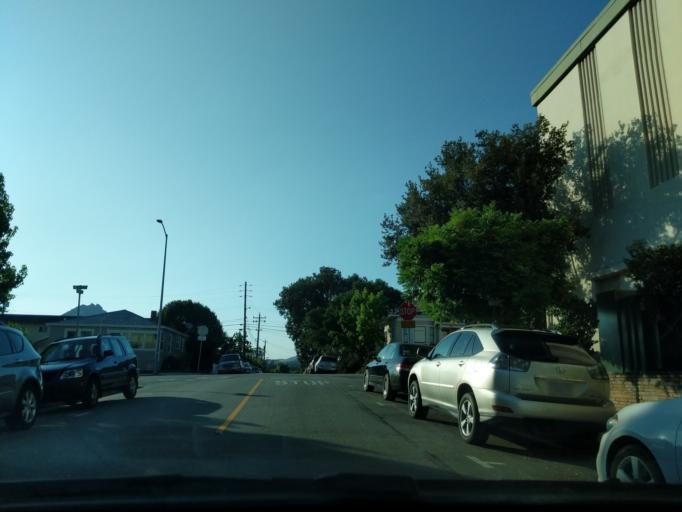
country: US
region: California
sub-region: San Luis Obispo County
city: San Luis Obispo
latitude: 35.2827
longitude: -120.6636
